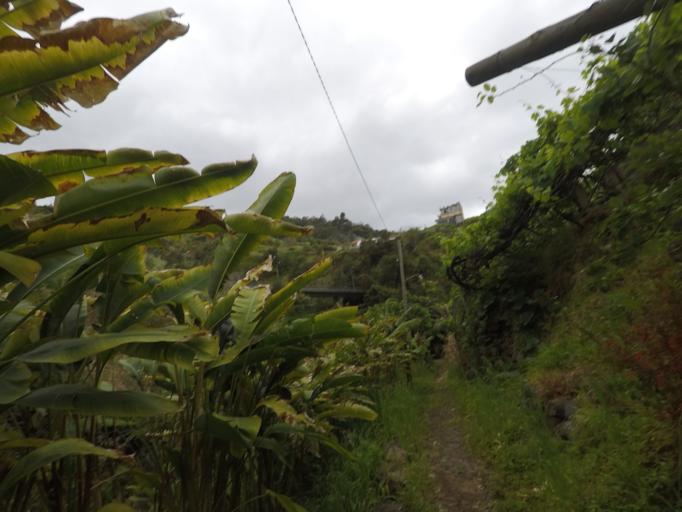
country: PT
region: Madeira
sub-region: Santana
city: Santana
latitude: 32.7575
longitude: -16.8290
